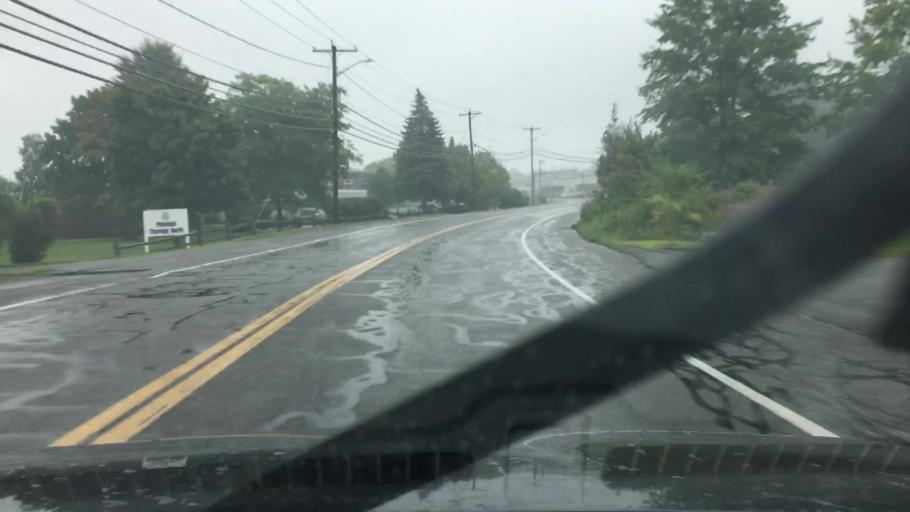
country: US
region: Massachusetts
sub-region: Essex County
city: Newburyport
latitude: 42.7987
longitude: -70.8866
